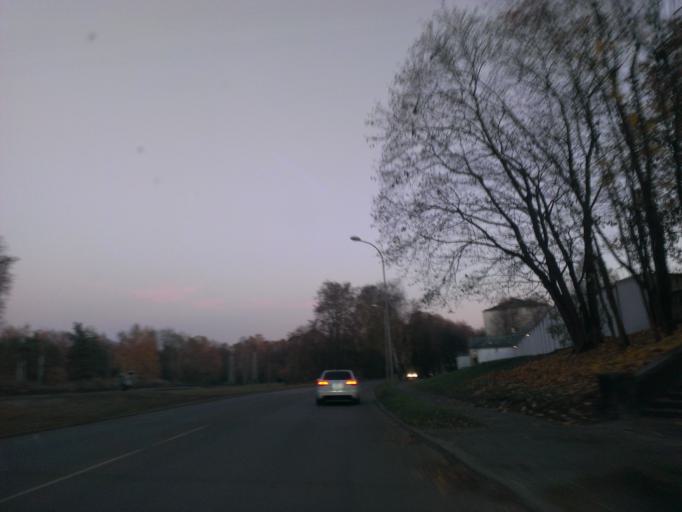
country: LV
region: Riga
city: Riga
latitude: 56.9806
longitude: 24.1403
